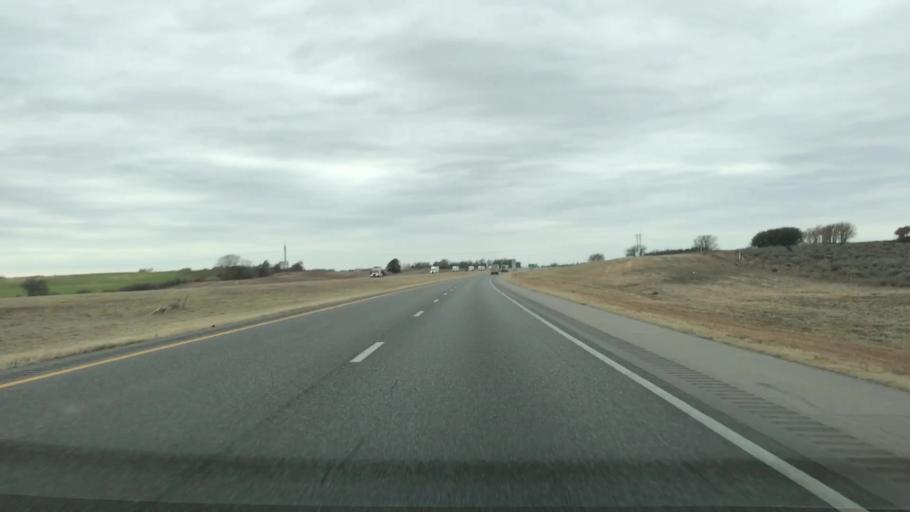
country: US
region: Oklahoma
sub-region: Beckham County
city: Erick
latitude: 35.2272
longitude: -99.9214
